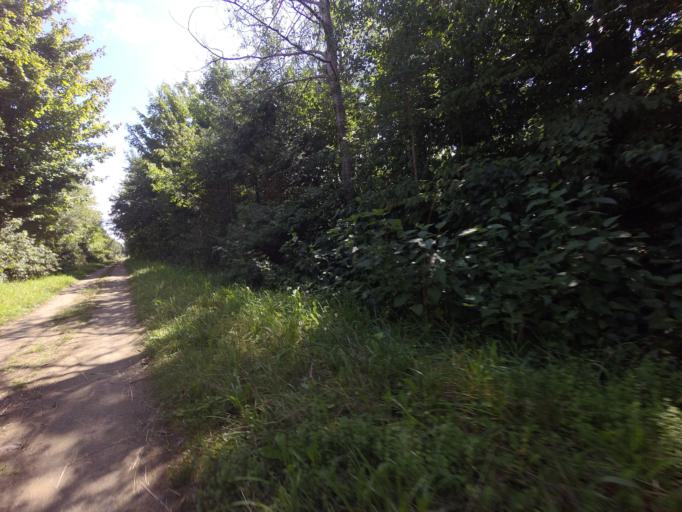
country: CA
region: Ontario
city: Orangeville
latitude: 43.7928
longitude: -80.3010
